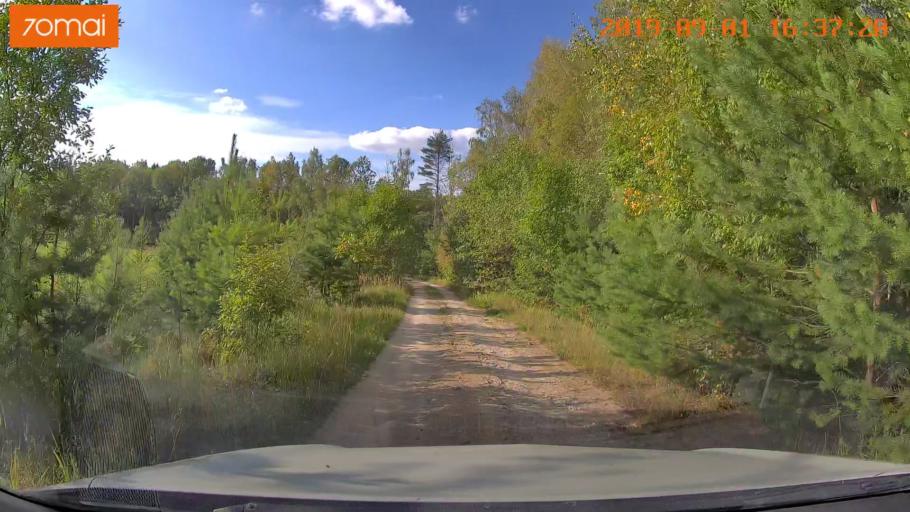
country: RU
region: Kaluga
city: Maloyaroslavets
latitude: 54.9495
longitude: 36.4747
